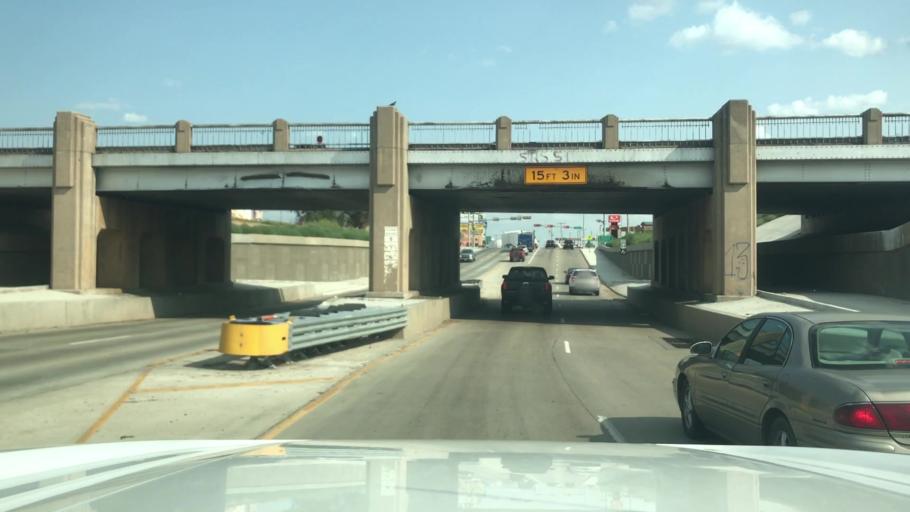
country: US
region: Texas
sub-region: Dallam County
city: Dalhart
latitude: 36.0666
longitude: -102.5223
